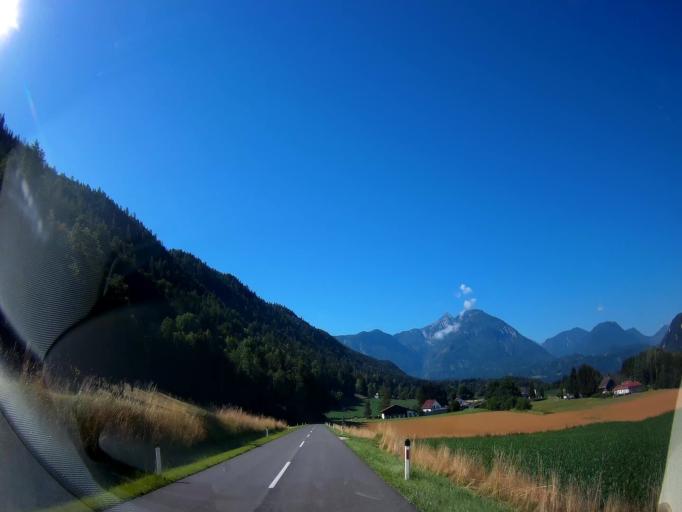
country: AT
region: Carinthia
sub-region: Politischer Bezirk Volkermarkt
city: Gallizien
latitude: 46.5975
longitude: 14.5294
